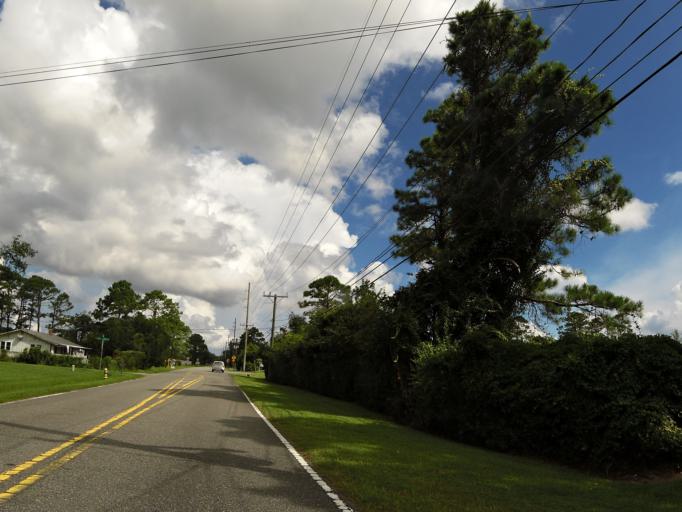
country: US
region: Florida
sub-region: Nassau County
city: Fernandina Beach
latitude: 30.6242
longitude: -81.4660
